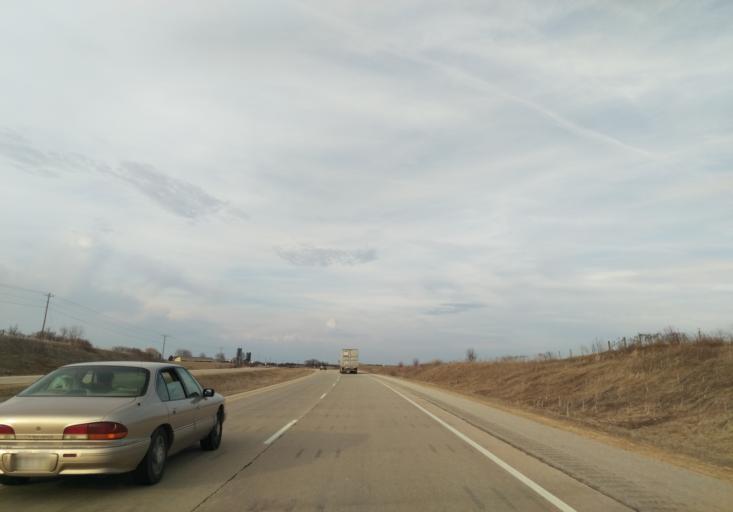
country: US
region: Wisconsin
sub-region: Iowa County
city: Dodgeville
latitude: 42.9823
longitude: -90.0154
